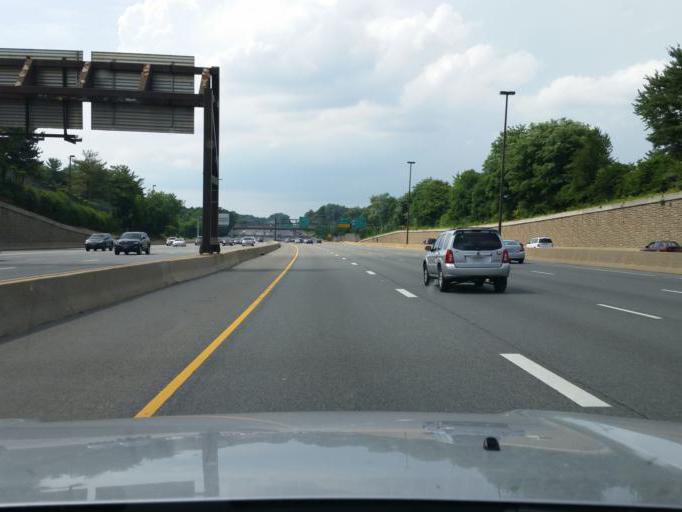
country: US
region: Maryland
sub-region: Montgomery County
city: Gaithersburg
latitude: 39.1267
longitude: -77.2021
